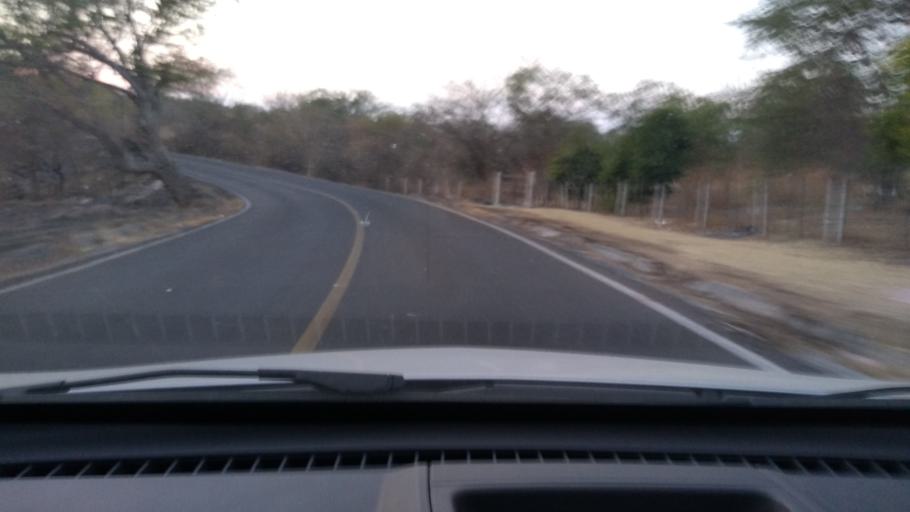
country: MX
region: Morelos
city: Coatetelco
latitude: 18.7248
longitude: -99.2957
